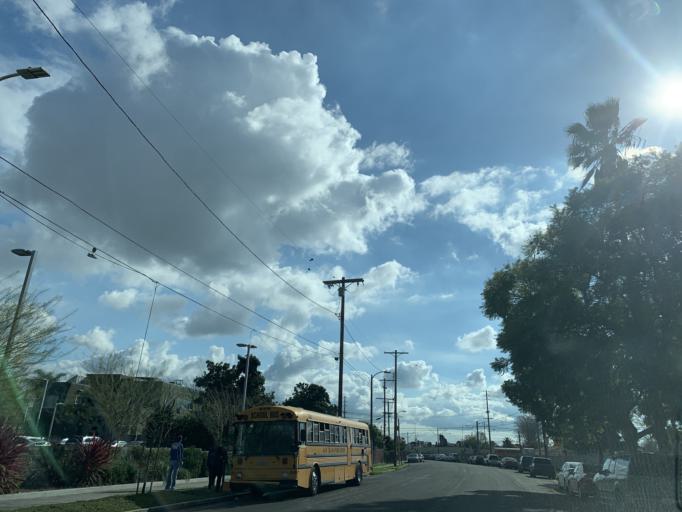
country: US
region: California
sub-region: Los Angeles County
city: Willowbrook
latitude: 33.9395
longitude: -118.2428
